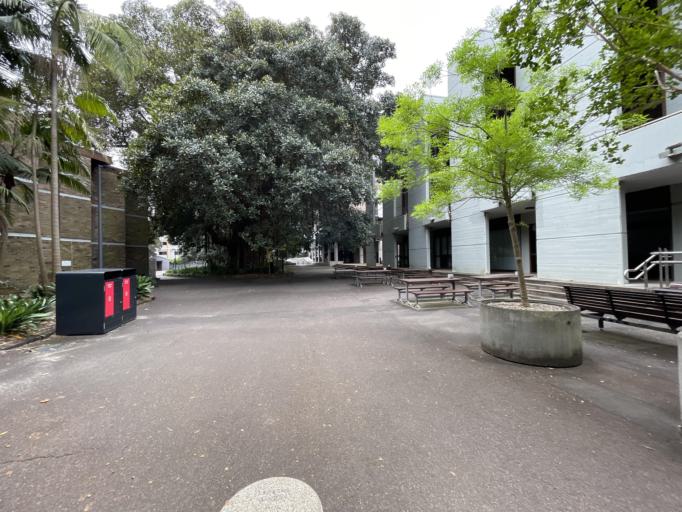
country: AU
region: New South Wales
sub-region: Randwick
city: Kingsford
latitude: -33.9167
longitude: 151.2311
